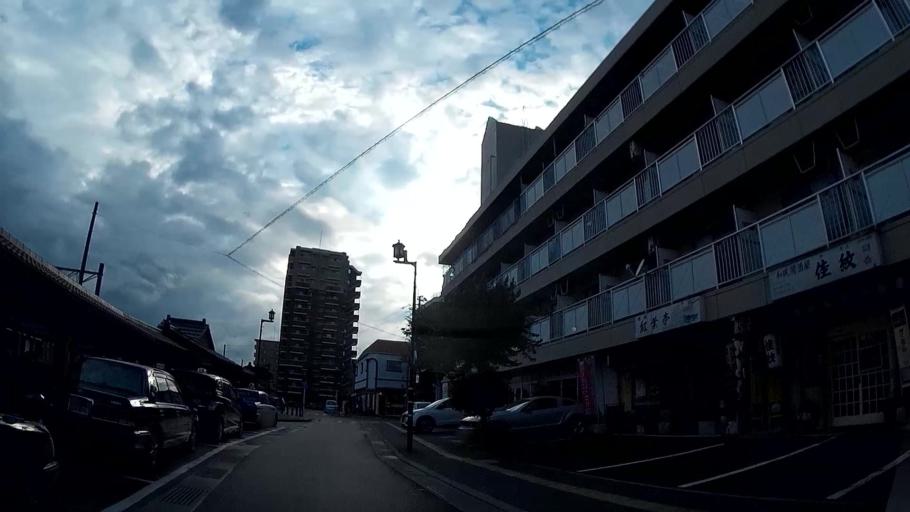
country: JP
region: Kumamoto
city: Ozu
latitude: 32.8777
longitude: 130.8667
